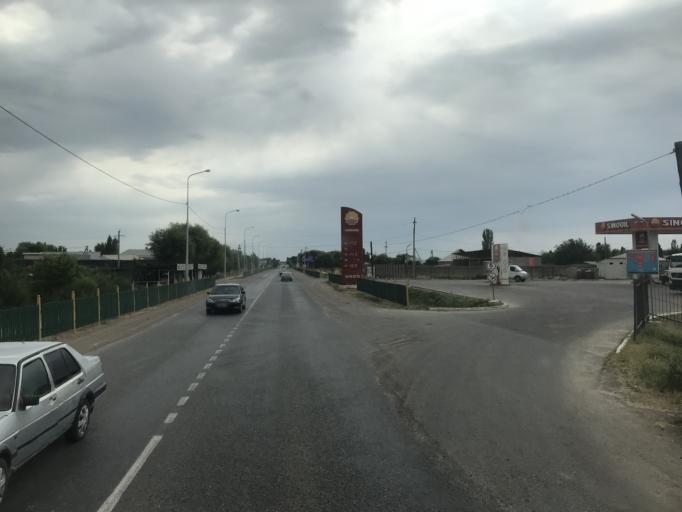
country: KZ
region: Ongtustik Qazaqstan
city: Saryaghash
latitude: 41.3539
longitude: 68.9699
